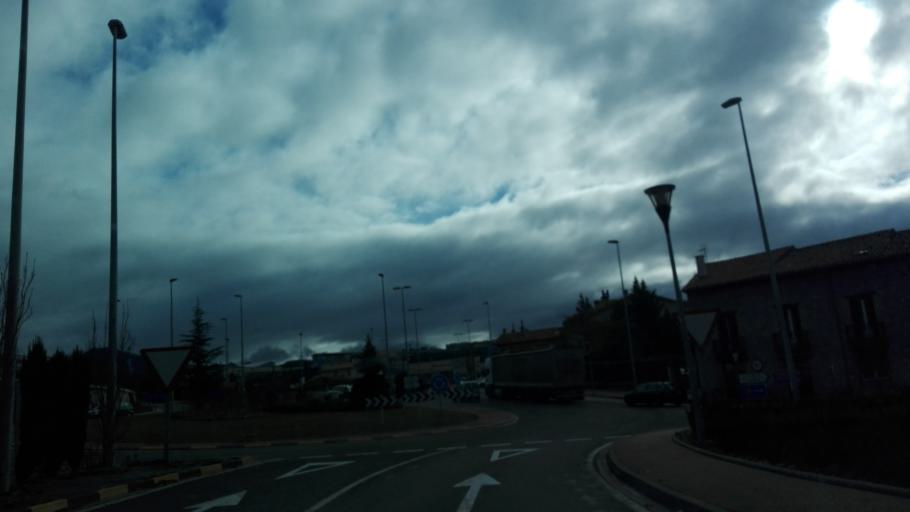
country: ES
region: Navarre
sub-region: Provincia de Navarra
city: Egues-Uharte
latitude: 42.8328
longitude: -1.5861
